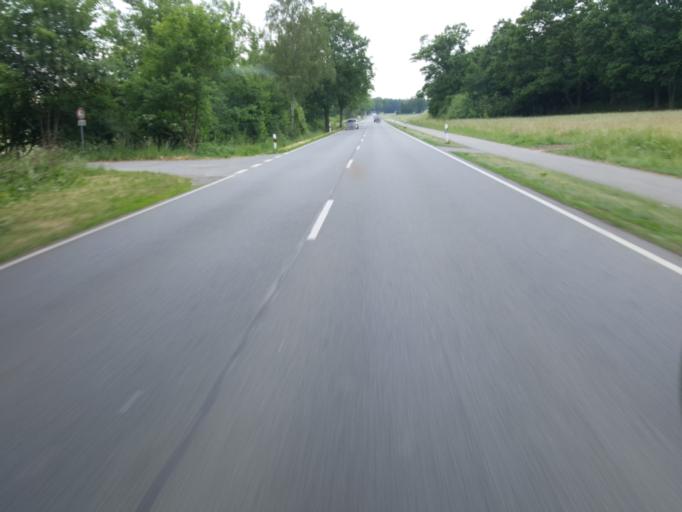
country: DE
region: Lower Saxony
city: Leese
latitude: 52.4700
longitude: 9.1416
